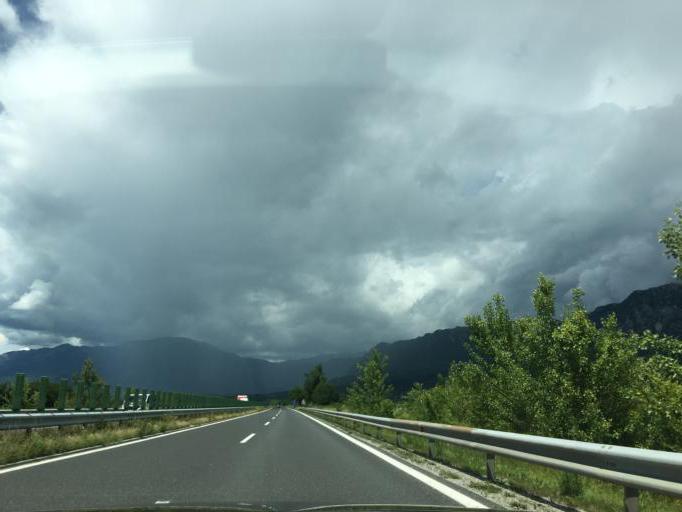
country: SI
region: Vipava
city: Vipava
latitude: 45.8536
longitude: 13.9450
